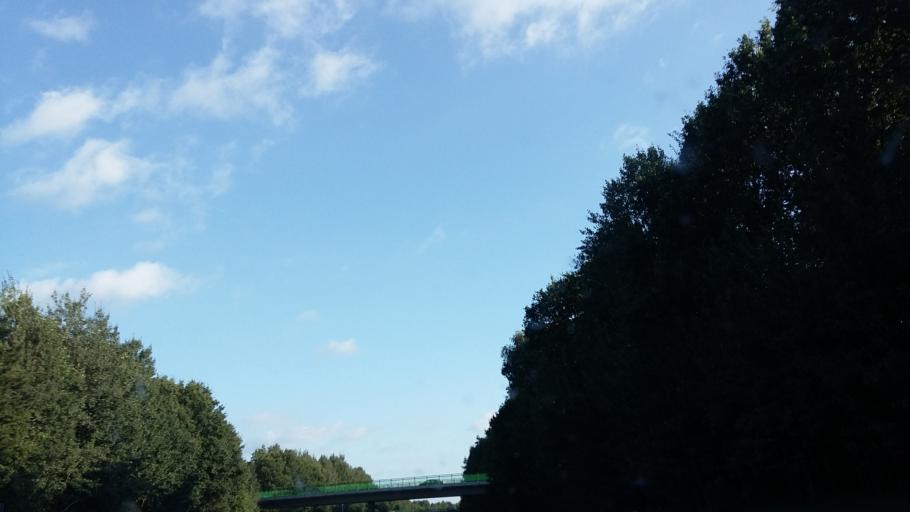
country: DE
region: Lower Saxony
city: Schiffdorf
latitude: 53.5188
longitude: 8.6265
